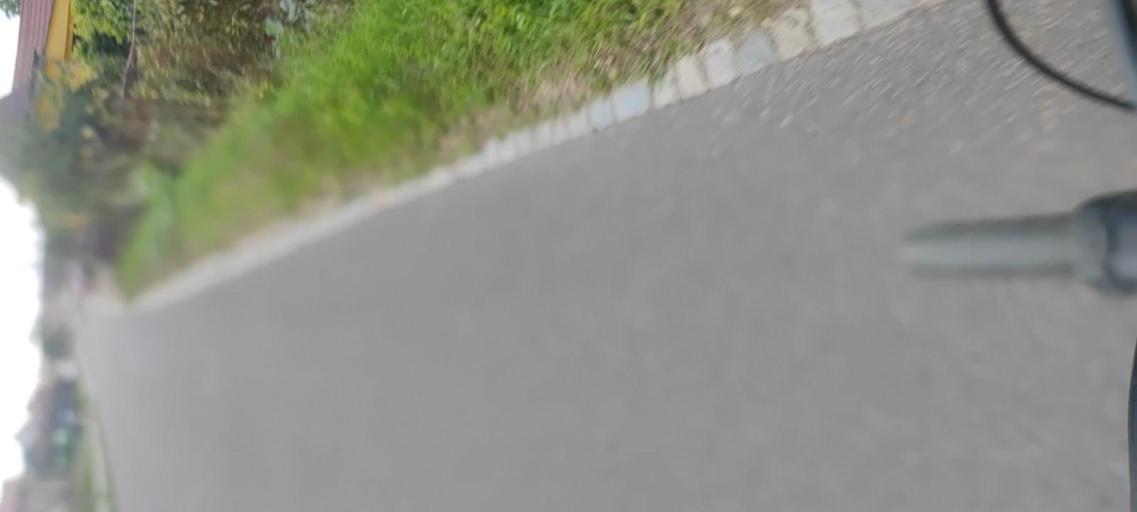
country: CZ
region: South Moravian
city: Dobsice
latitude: 48.8376
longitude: 16.0779
